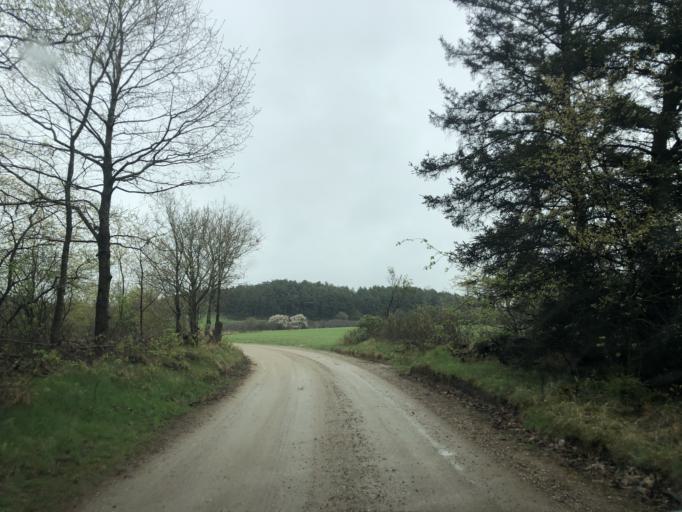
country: DK
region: Central Jutland
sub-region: Lemvig Kommune
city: Lemvig
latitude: 56.4452
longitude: 8.3854
